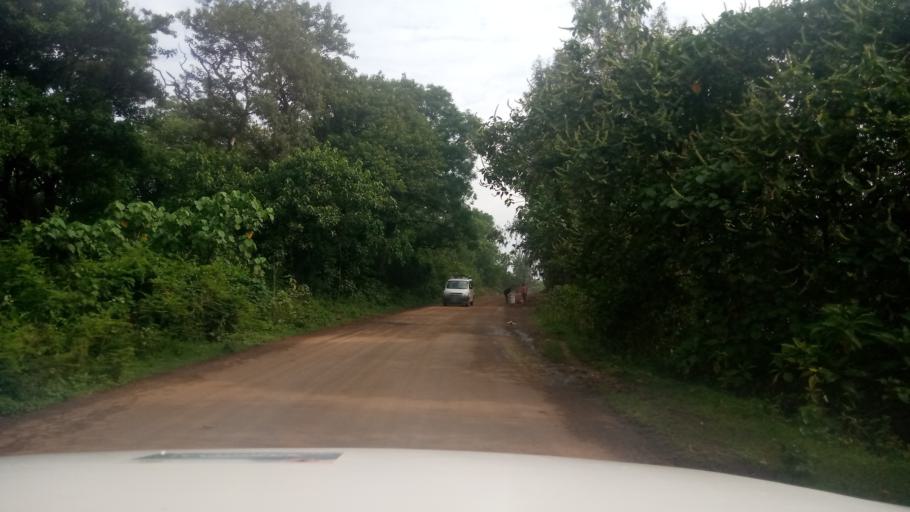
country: ET
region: Oromiya
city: Agaro
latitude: 7.8455
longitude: 36.6578
